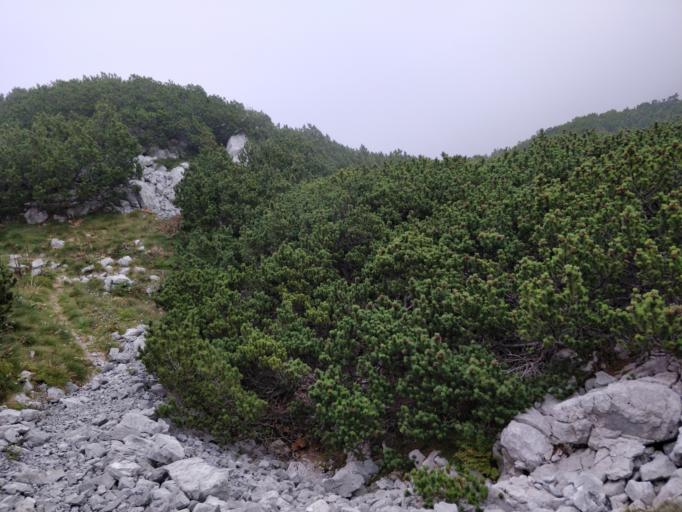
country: HR
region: Zadarska
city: Starigrad
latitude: 44.3585
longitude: 15.5241
